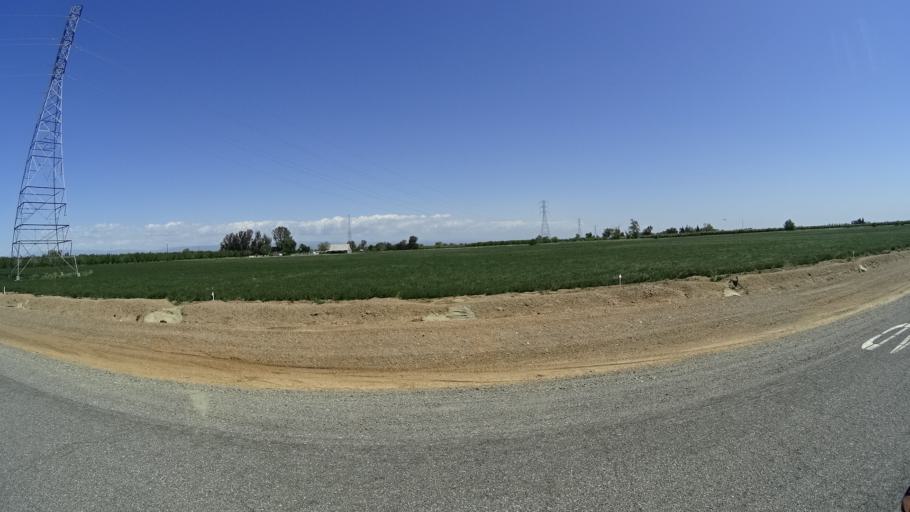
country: US
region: California
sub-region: Glenn County
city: Orland
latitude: 39.7962
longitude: -122.1785
